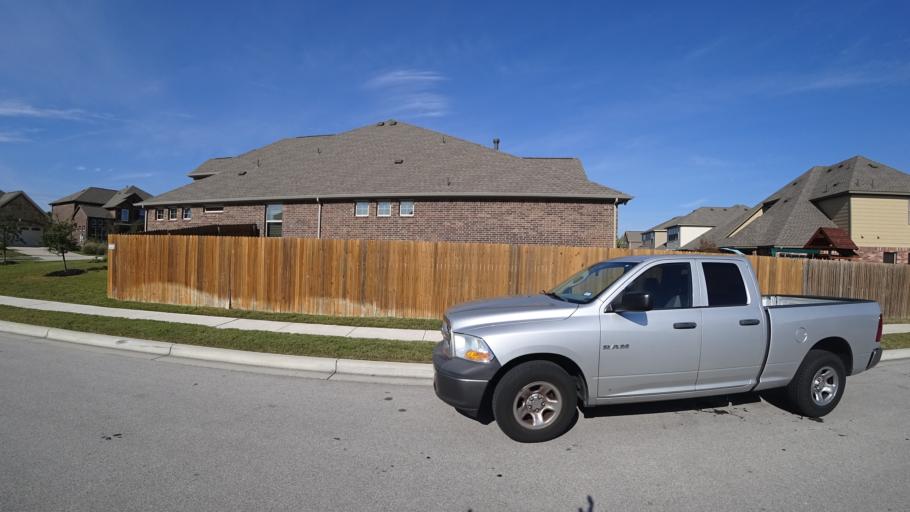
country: US
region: Texas
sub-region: Travis County
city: Barton Creek
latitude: 30.2318
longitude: -97.9106
